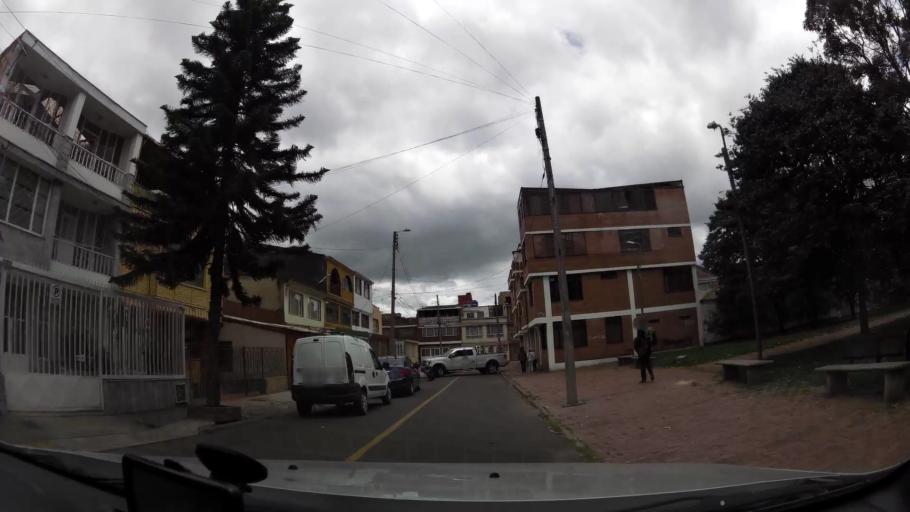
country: CO
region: Bogota D.C.
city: Bogota
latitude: 4.6080
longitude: -74.1171
